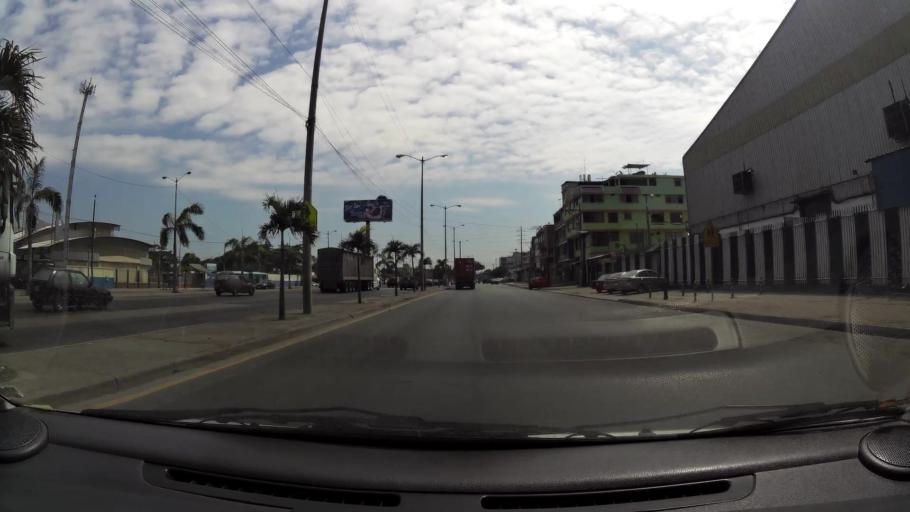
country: EC
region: Guayas
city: Guayaquil
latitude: -2.2474
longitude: -79.8949
